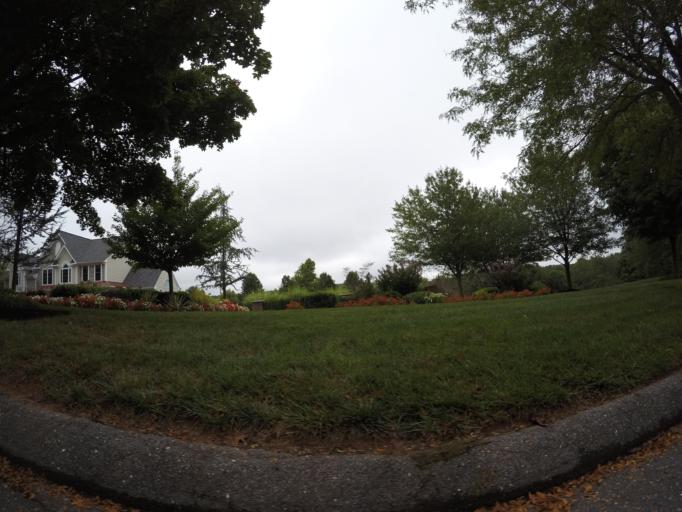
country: US
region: Maryland
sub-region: Carroll County
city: Sykesville
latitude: 39.3327
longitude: -77.0475
